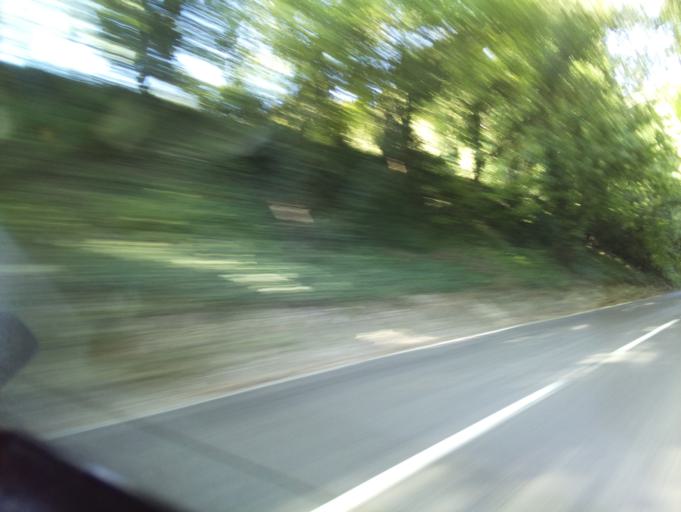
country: GB
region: England
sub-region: Hampshire
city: Four Marks
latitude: 51.0410
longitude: -1.0664
